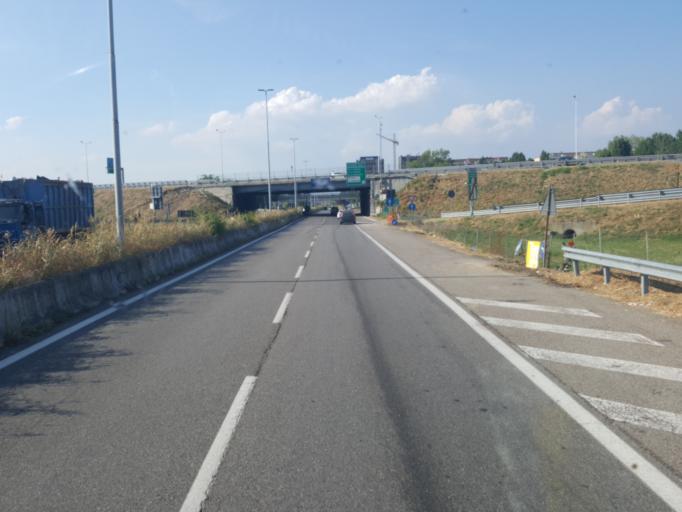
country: IT
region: Lombardy
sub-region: Citta metropolitana di Milano
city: Noverasco-Sporting Mirasole
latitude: 45.3887
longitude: 9.2126
